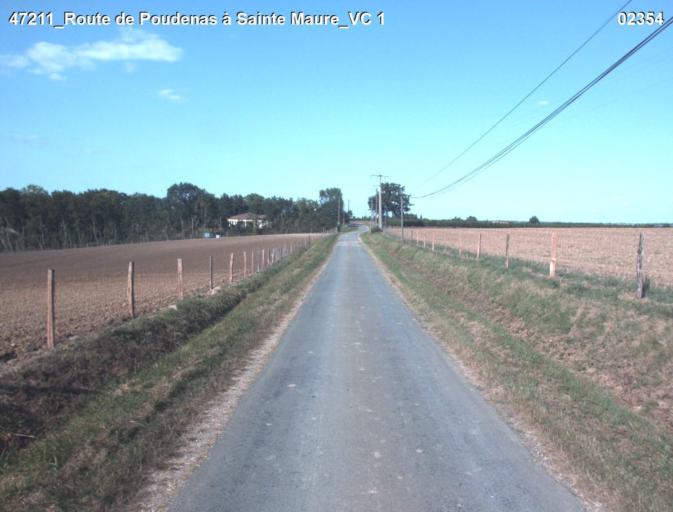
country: FR
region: Aquitaine
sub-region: Departement du Lot-et-Garonne
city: Mezin
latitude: 44.0295
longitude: 0.2031
